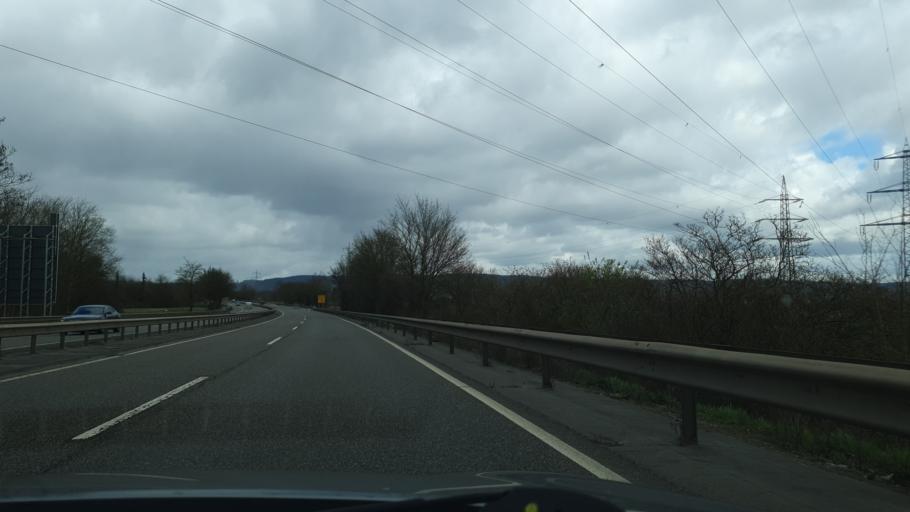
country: DE
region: Rheinland-Pfalz
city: Neuwied
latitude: 50.4241
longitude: 7.4859
